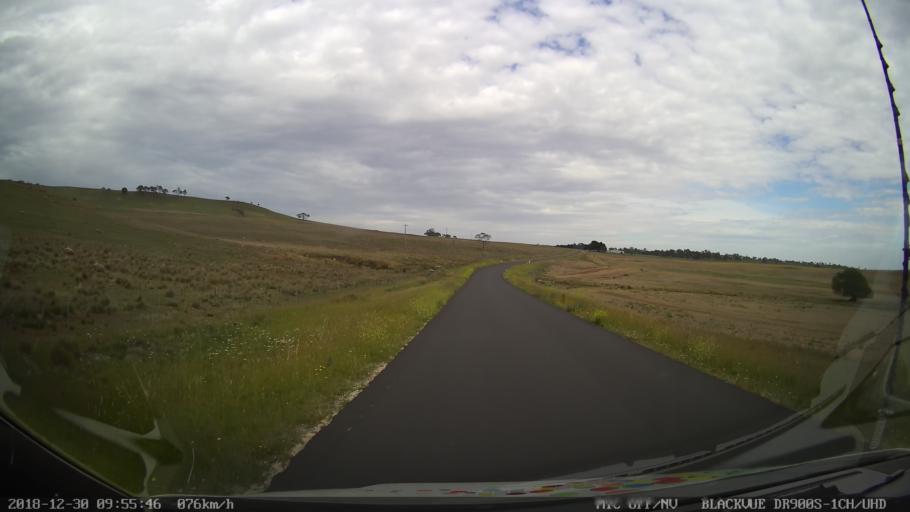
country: AU
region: New South Wales
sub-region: Cooma-Monaro
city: Cooma
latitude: -36.5219
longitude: 149.2603
